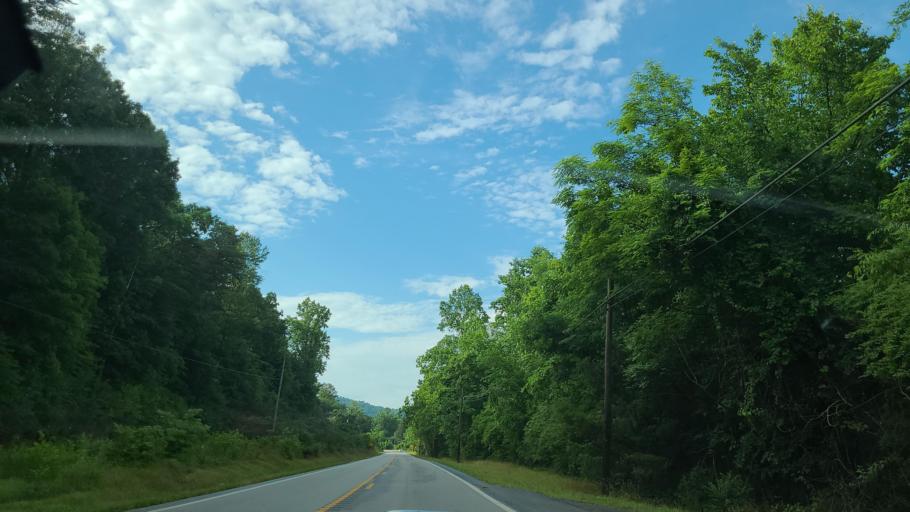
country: US
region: Kentucky
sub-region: Whitley County
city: Williamsburg
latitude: 36.7287
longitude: -84.1293
